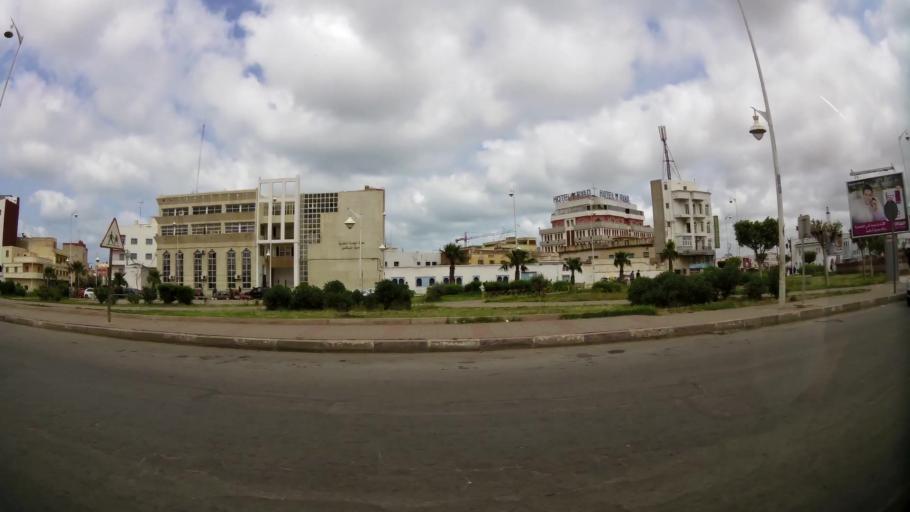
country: MA
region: Oriental
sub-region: Nador
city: Nador
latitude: 35.1801
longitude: -2.9286
